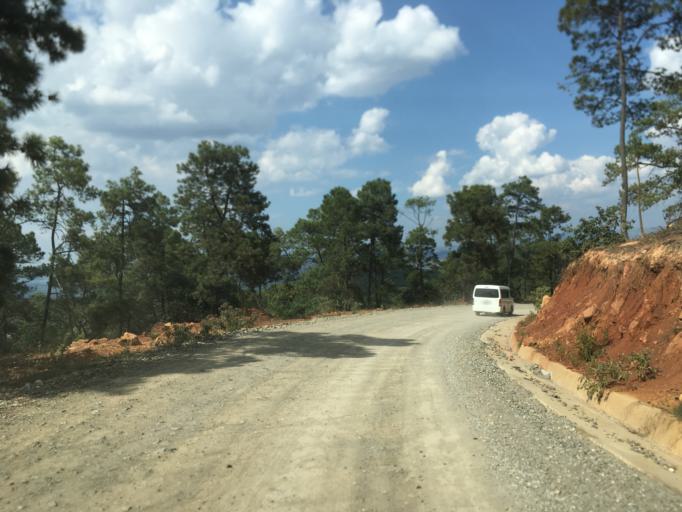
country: MX
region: Oaxaca
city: Santiago Tilantongo
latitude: 17.2081
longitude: -97.2781
